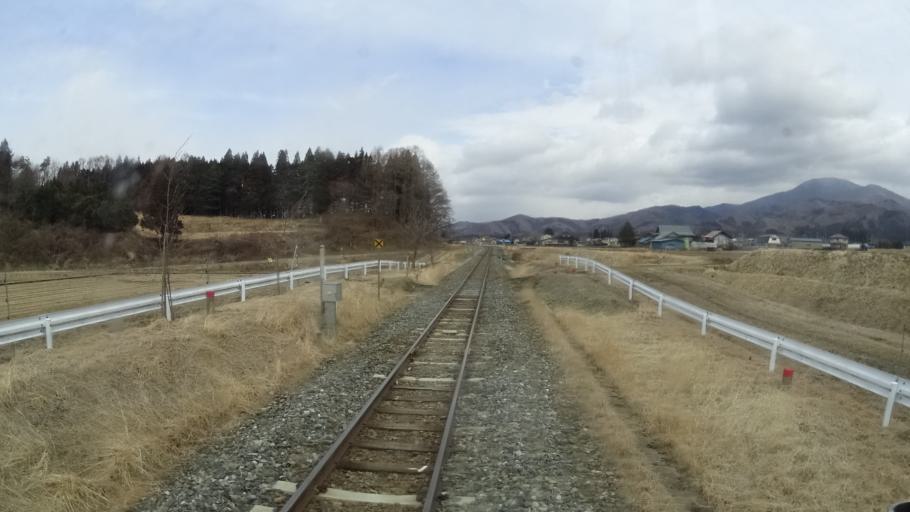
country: JP
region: Iwate
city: Tono
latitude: 39.2755
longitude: 141.5905
